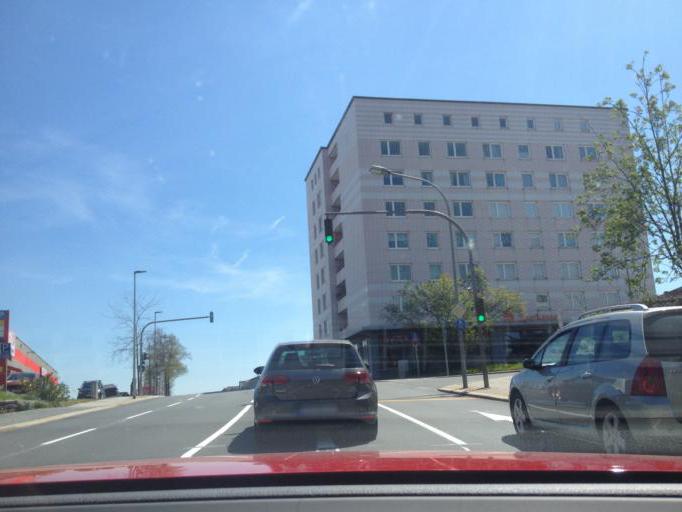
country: DE
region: Bavaria
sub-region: Upper Franconia
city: Hof
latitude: 50.3097
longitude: 11.9115
